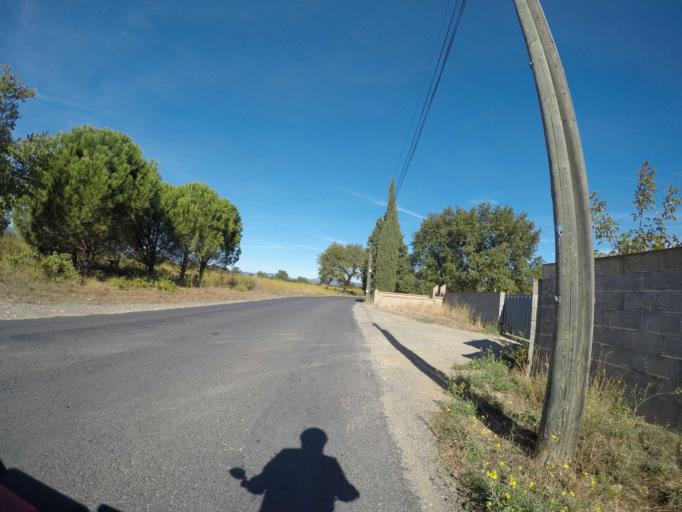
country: FR
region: Languedoc-Roussillon
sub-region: Departement des Pyrenees-Orientales
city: Ponteilla
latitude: 42.6417
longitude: 2.8031
